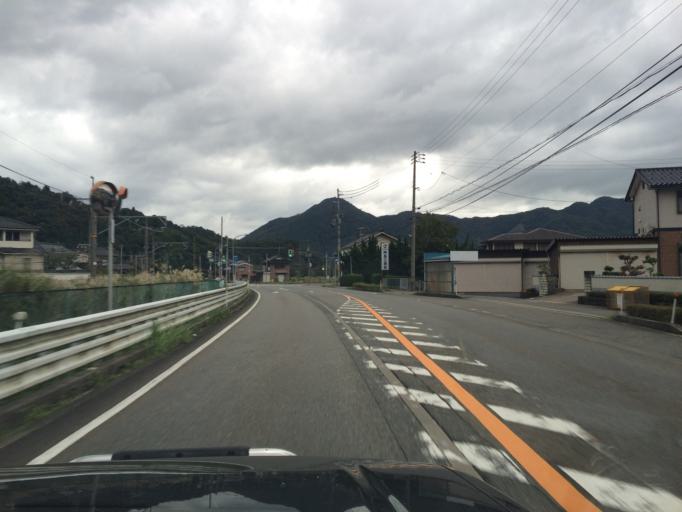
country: JP
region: Hyogo
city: Toyooka
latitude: 35.4235
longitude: 134.7902
